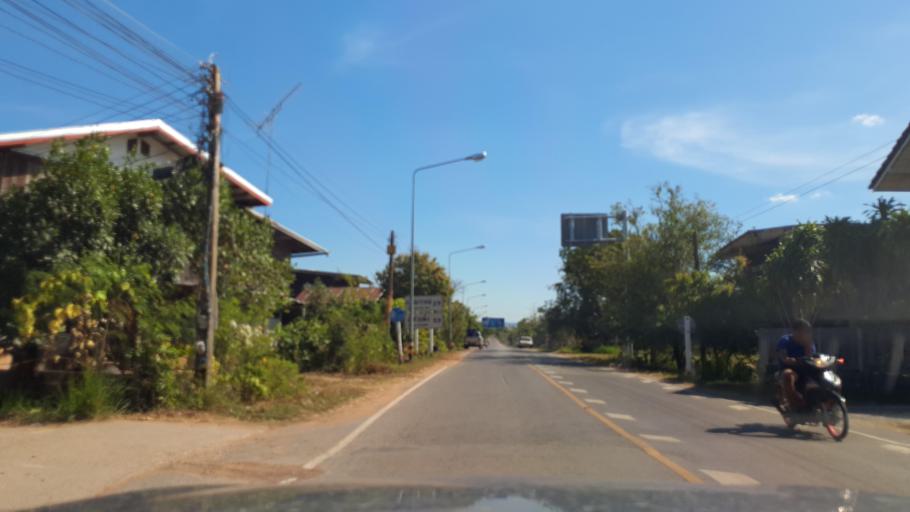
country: TH
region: Kalasin
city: Khao Wong
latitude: 16.7328
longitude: 104.0964
